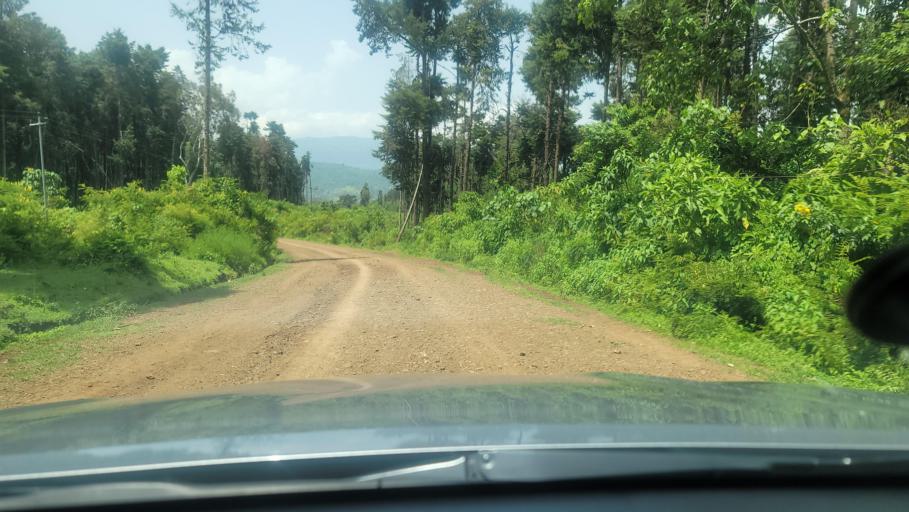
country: ET
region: Oromiya
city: Agaro
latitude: 7.7944
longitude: 36.4172
